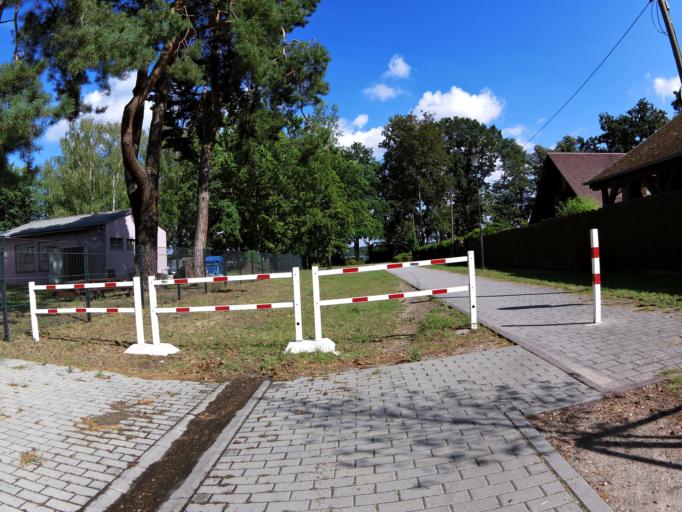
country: DE
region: Brandenburg
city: Storkow
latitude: 52.2512
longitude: 13.9470
